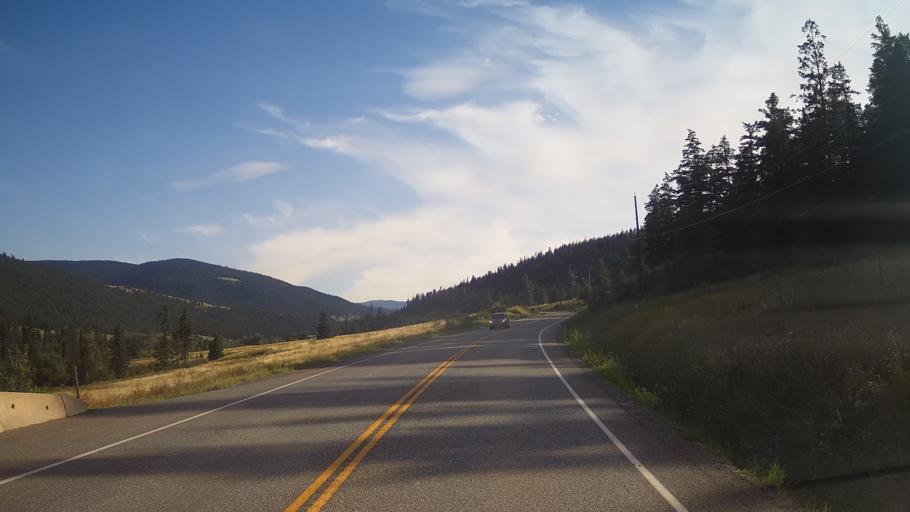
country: CA
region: British Columbia
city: Cache Creek
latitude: 50.8556
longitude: -121.5327
